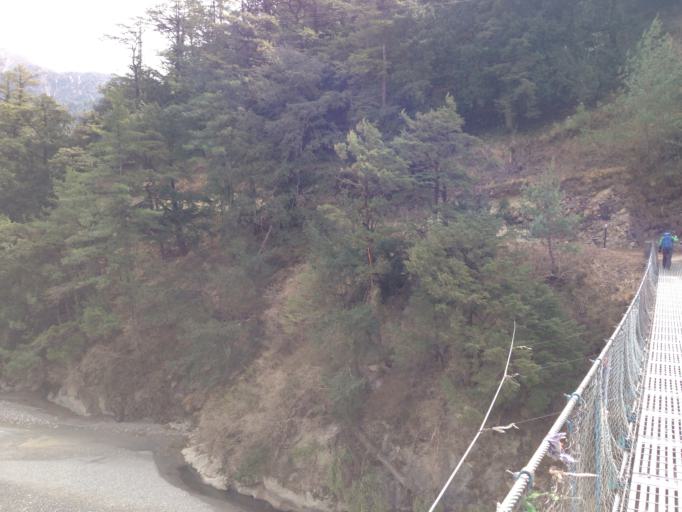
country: NP
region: Western Region
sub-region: Dhawalagiri Zone
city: Jomsom
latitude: 28.6719
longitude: 83.5975
